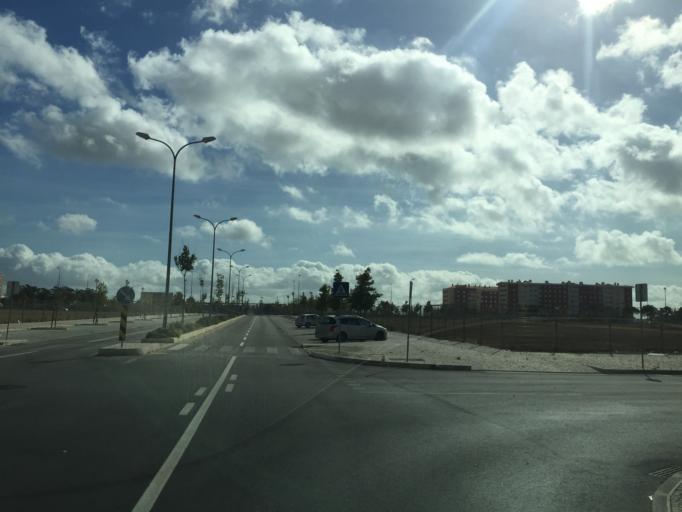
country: PT
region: Lisbon
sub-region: Odivelas
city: Olival do Basto
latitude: 38.7766
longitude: -9.1499
